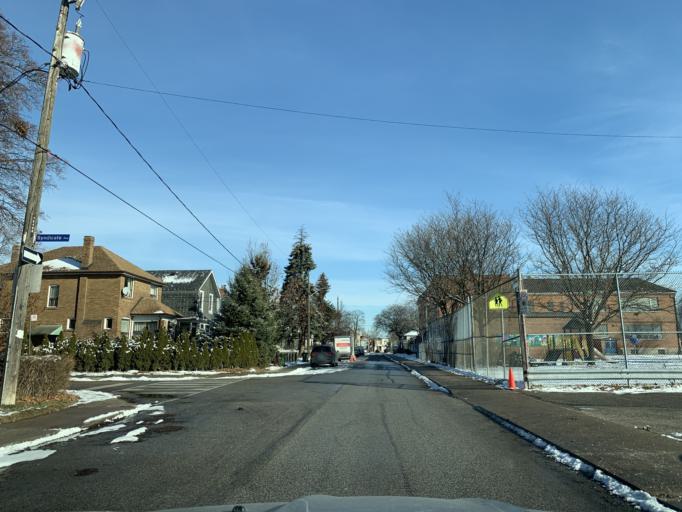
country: CA
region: Ontario
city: Toronto
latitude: 43.6843
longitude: -79.4886
